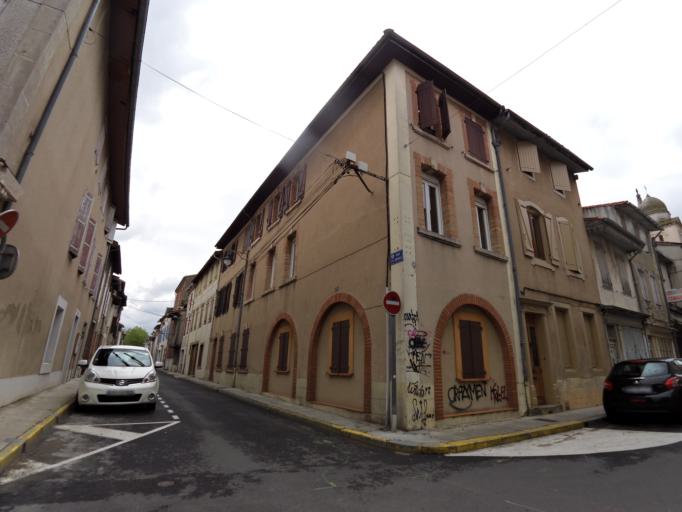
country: FR
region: Midi-Pyrenees
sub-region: Departement de la Haute-Garonne
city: Revel
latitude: 43.4576
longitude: 2.0044
